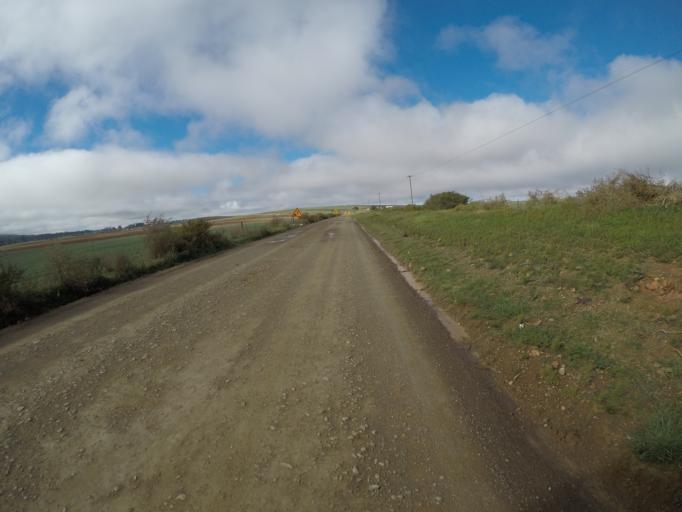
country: ZA
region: Western Cape
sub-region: Cape Winelands District Municipality
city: Ashton
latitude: -34.1516
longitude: 19.8818
